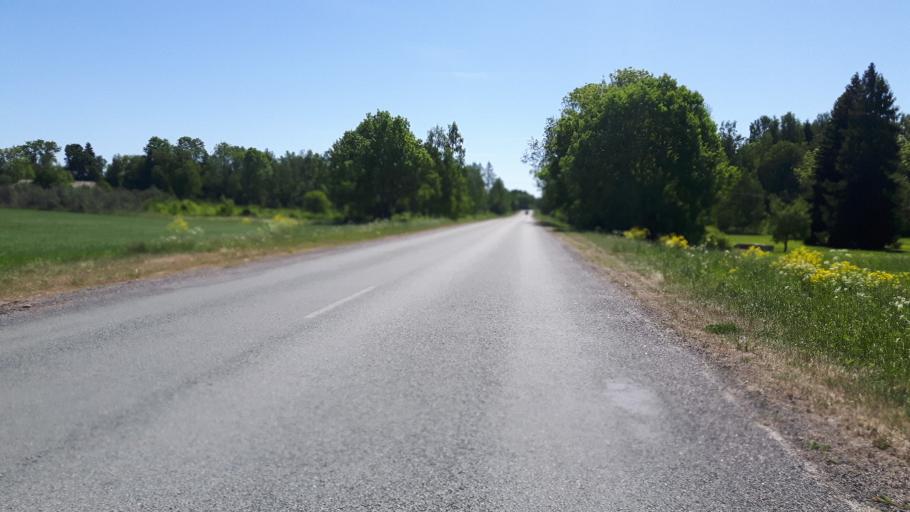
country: EE
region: Harju
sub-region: Kuusalu vald
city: Kuusalu
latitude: 59.4640
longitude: 25.4490
